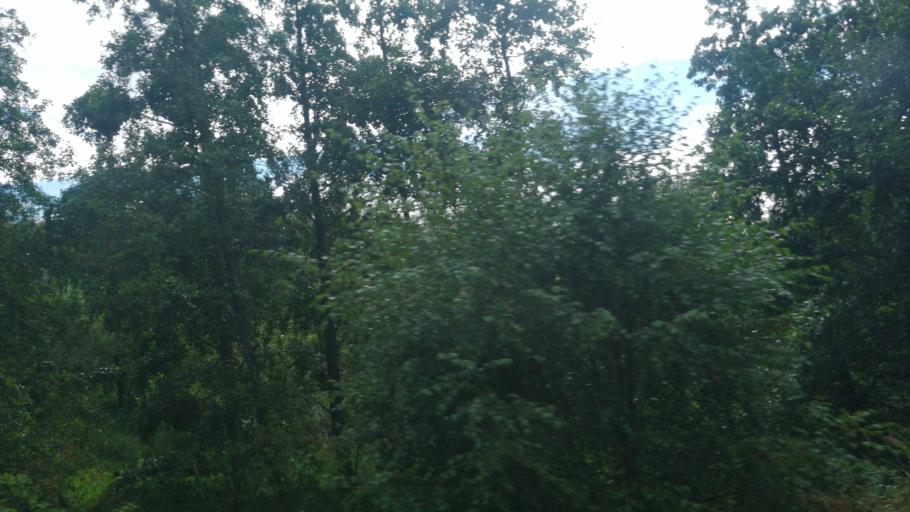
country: GB
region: Scotland
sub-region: Aberdeenshire
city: Insch
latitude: 57.3373
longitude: -2.6424
